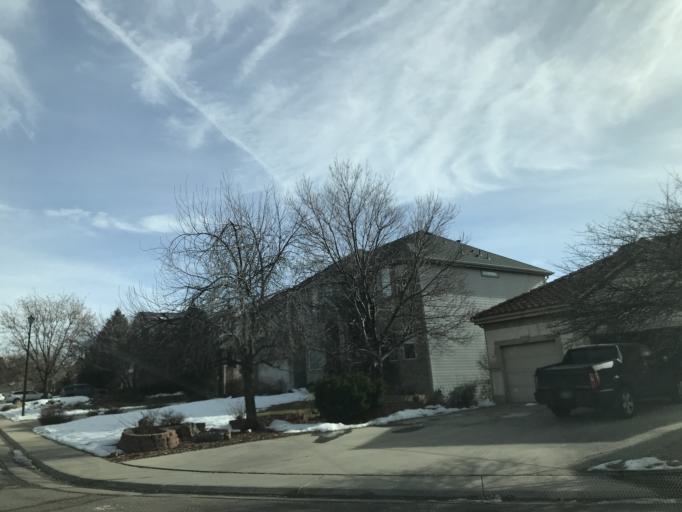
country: US
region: Colorado
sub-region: Arapahoe County
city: Columbine Valley
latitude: 39.5992
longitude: -105.0190
